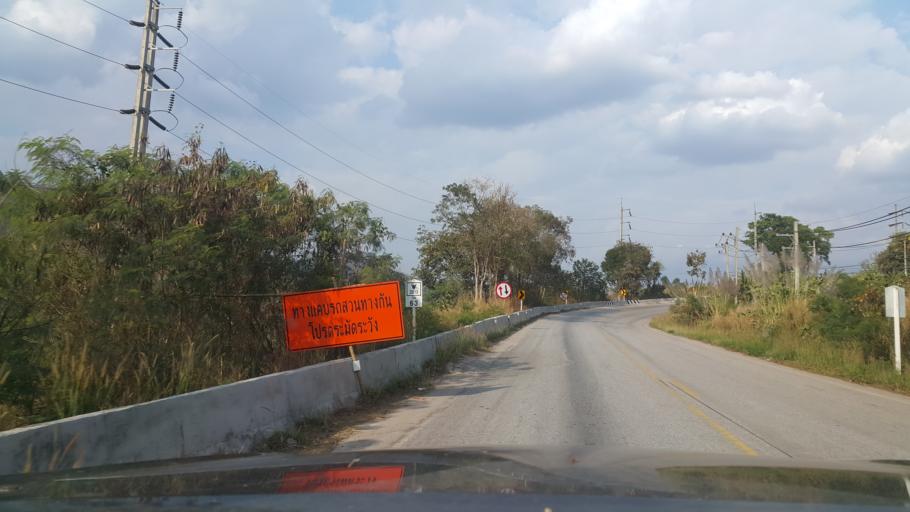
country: TH
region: Loei
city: Dan Sai
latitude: 17.2338
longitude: 101.0976
